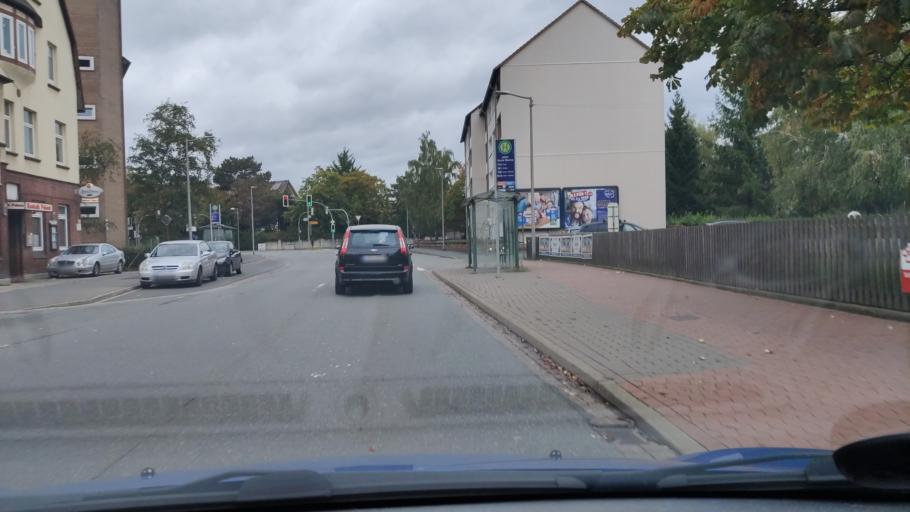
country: DE
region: Lower Saxony
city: Seelze
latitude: 52.3968
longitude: 9.6480
